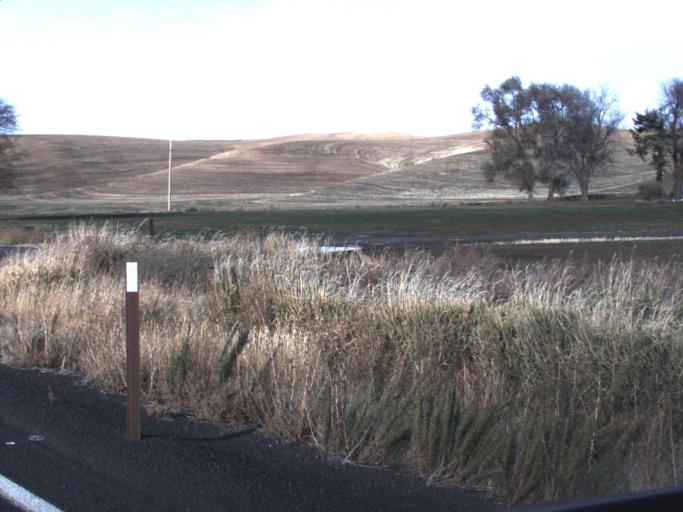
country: US
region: Washington
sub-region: Whitman County
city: Colfax
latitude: 46.7627
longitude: -117.4258
